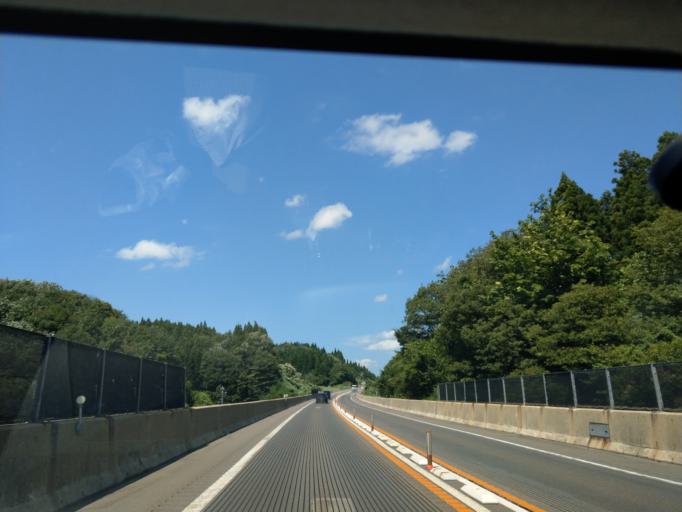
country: JP
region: Akita
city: Akita
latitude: 39.6769
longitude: 140.1860
